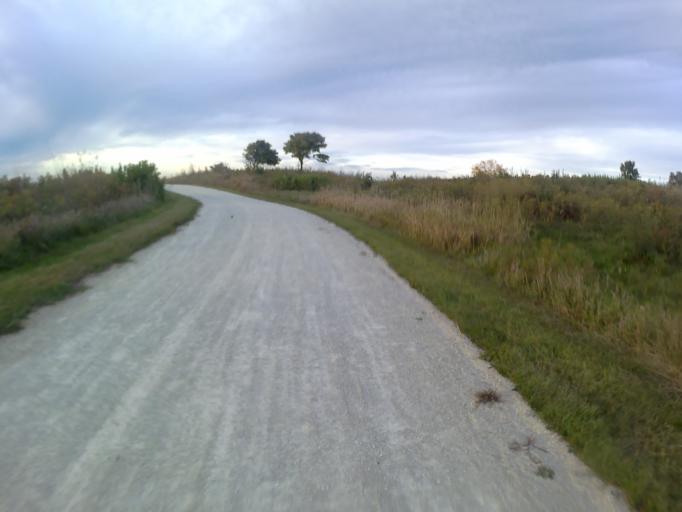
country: US
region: Illinois
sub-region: DuPage County
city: Lisle
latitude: 41.8273
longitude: -88.0948
